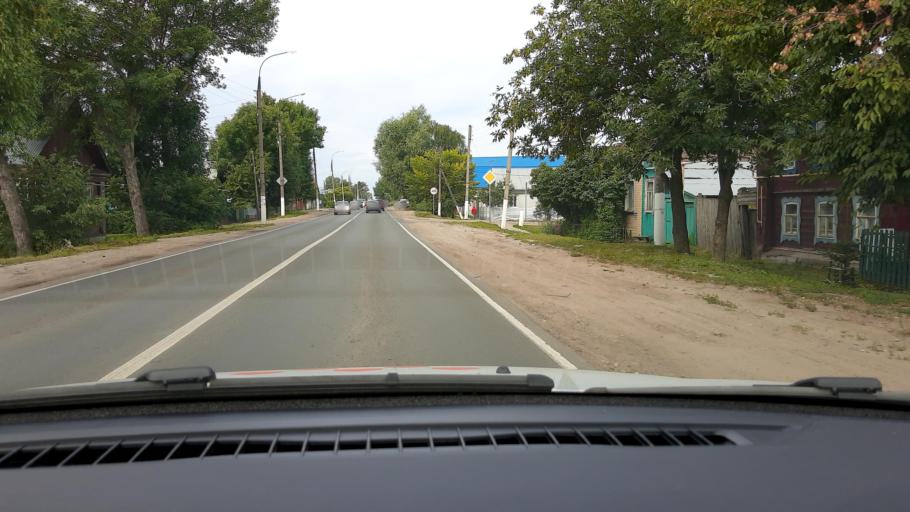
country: RU
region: Nizjnij Novgorod
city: Vyyezdnoye
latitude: 55.3836
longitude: 43.7928
